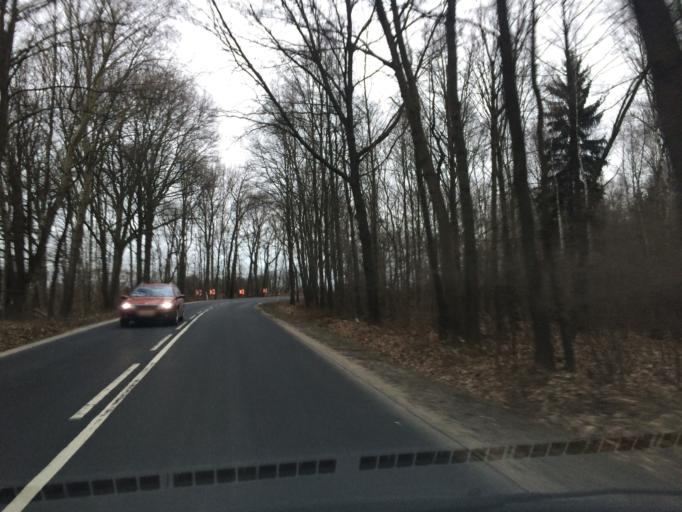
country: PL
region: Lower Silesian Voivodeship
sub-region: Powiat lubanski
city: Pisarzowice
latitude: 51.1537
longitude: 15.2663
